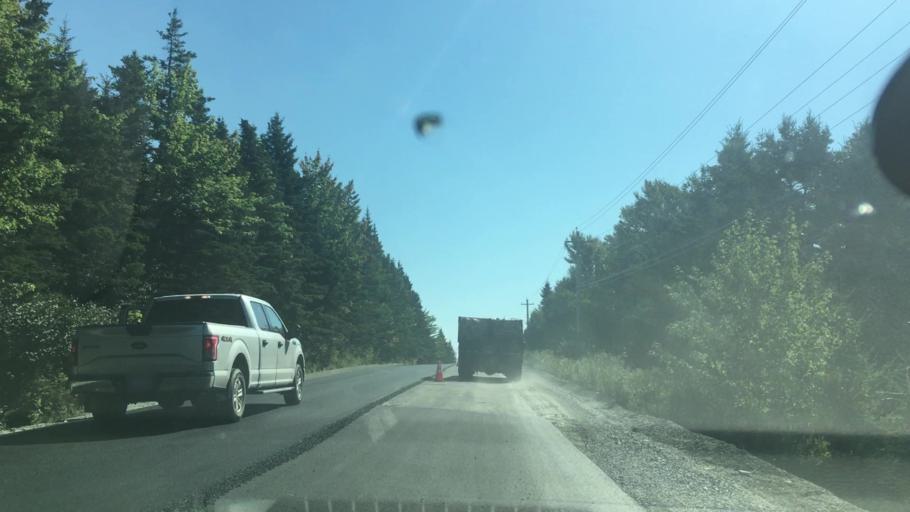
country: CA
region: Nova Scotia
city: New Glasgow
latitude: 44.9094
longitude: -62.5019
